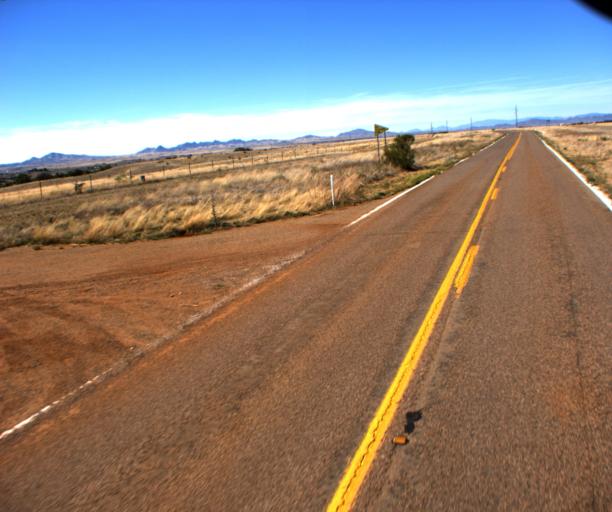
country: US
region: Arizona
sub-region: Cochise County
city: Huachuca City
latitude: 31.6438
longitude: -110.6010
